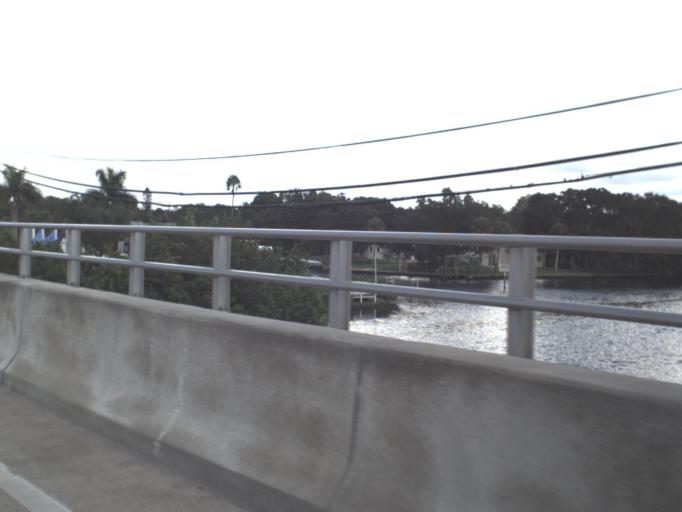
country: US
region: Florida
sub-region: Sarasota County
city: South Sarasota
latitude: 27.2734
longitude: -82.5305
